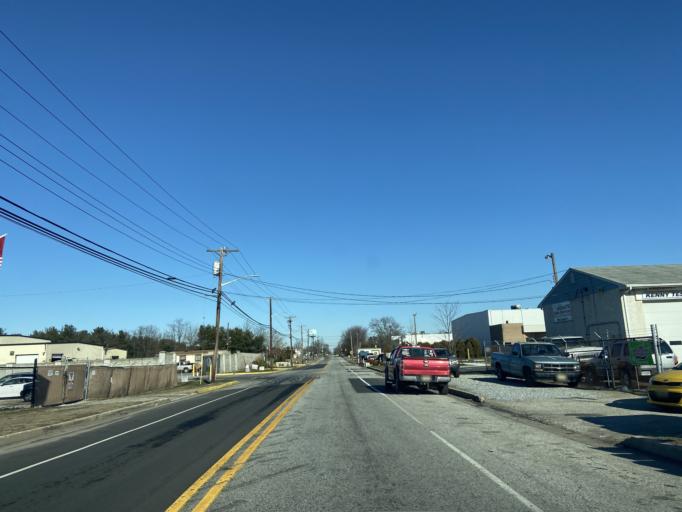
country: US
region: New Jersey
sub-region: Cumberland County
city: Vineland
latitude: 39.4883
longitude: -75.0614
